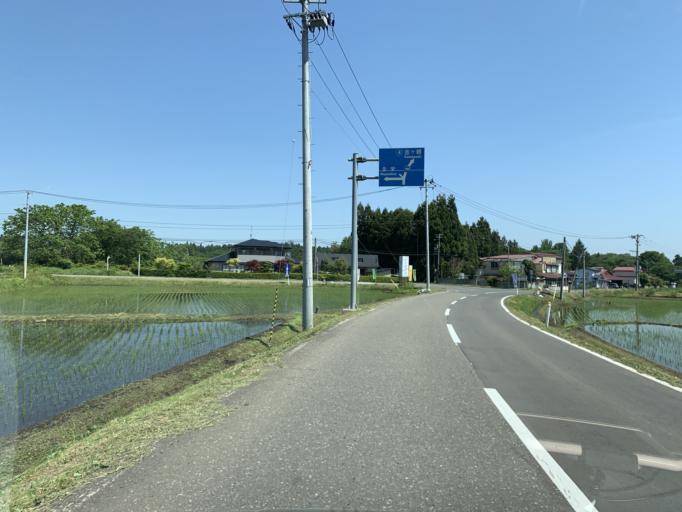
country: JP
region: Iwate
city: Mizusawa
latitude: 39.1716
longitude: 141.0606
